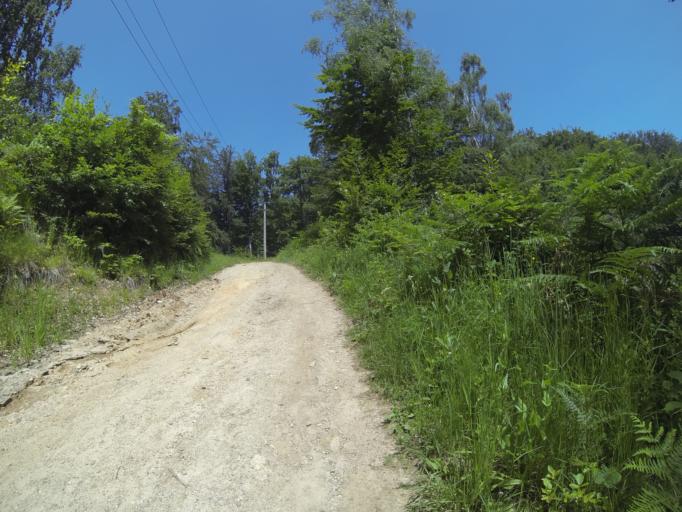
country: RO
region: Valcea
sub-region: Oras Baile Olanesti
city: Cheia
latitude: 45.2088
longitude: 24.2060
